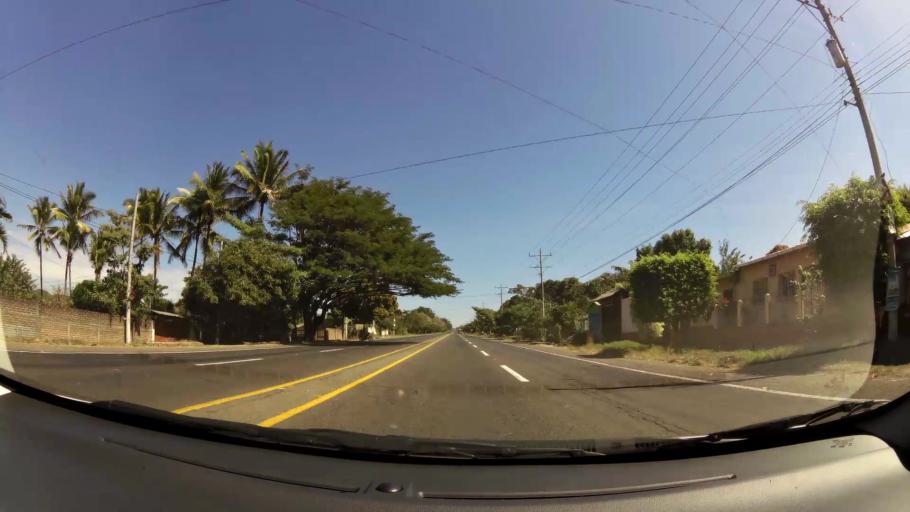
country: SV
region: Ahuachapan
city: Atiquizaya
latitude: 13.9725
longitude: -89.7171
